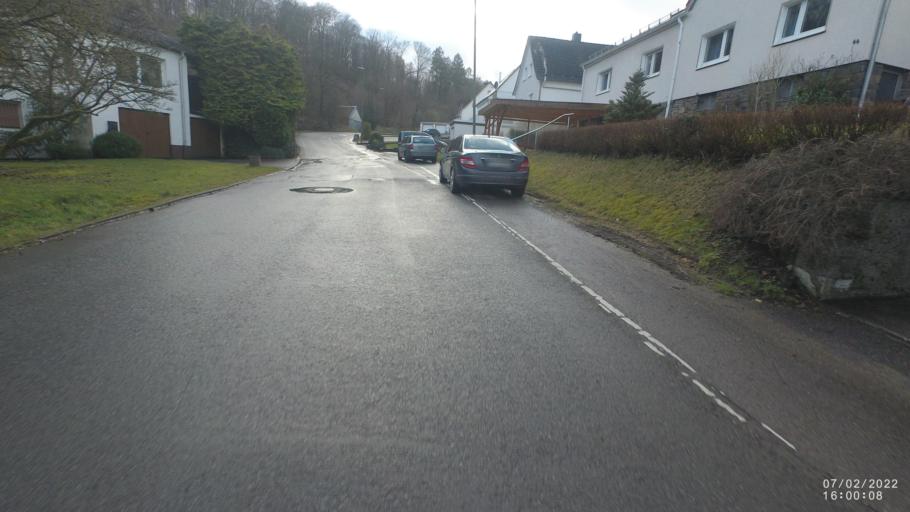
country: DE
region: North Rhine-Westphalia
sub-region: Regierungsbezirk Arnsberg
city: Luedenscheid
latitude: 51.2517
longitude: 7.6062
